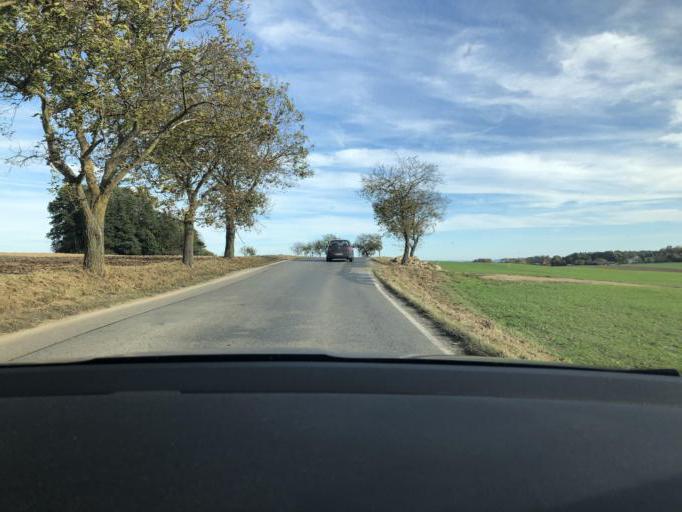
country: CZ
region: Central Bohemia
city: Postupice
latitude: 49.7687
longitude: 14.7763
